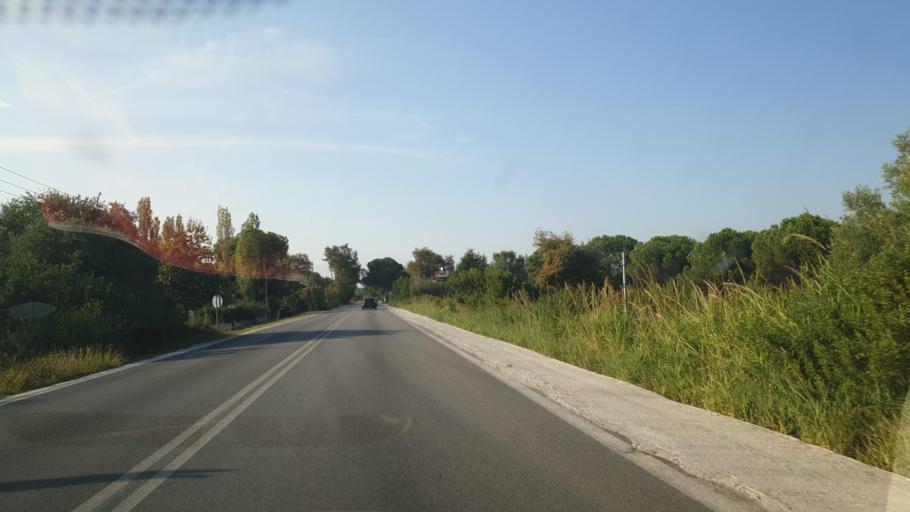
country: GR
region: Central Macedonia
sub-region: Nomos Chalkidikis
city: Agios Nikolaos
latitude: 40.1928
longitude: 23.7697
